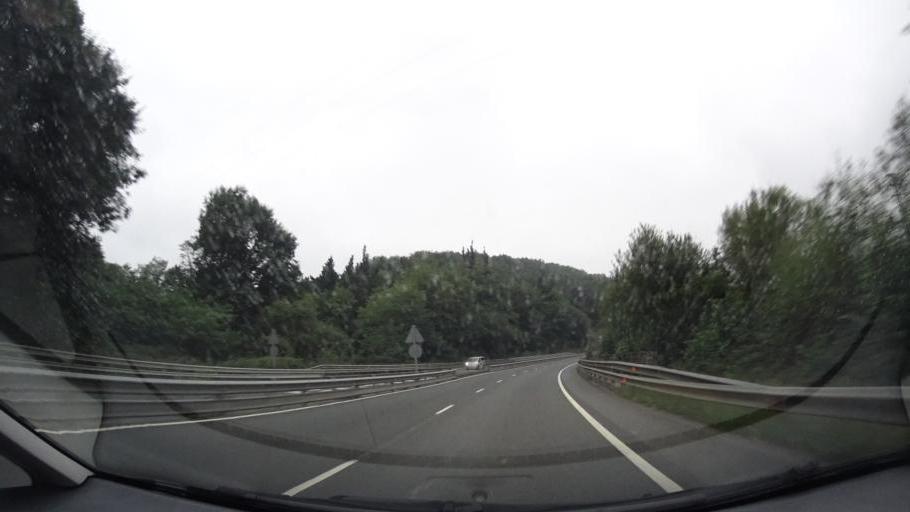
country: ES
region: Basque Country
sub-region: Bizkaia
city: Durango
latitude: 43.1671
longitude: -2.6438
